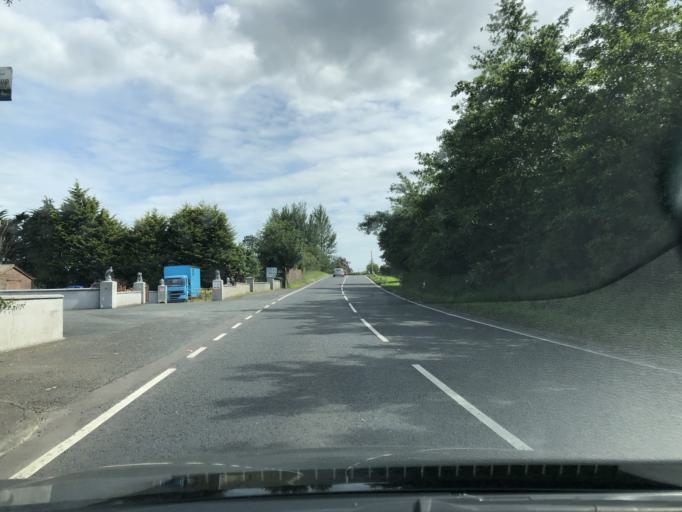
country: GB
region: Northern Ireland
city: Ballynahinch
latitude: 54.3790
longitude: -5.8698
